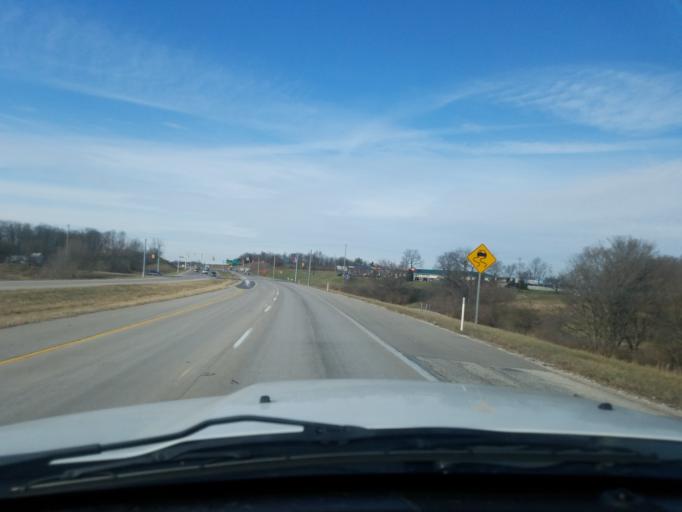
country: US
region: Indiana
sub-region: Monroe County
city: Bloomington
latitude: 39.1045
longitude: -86.5498
